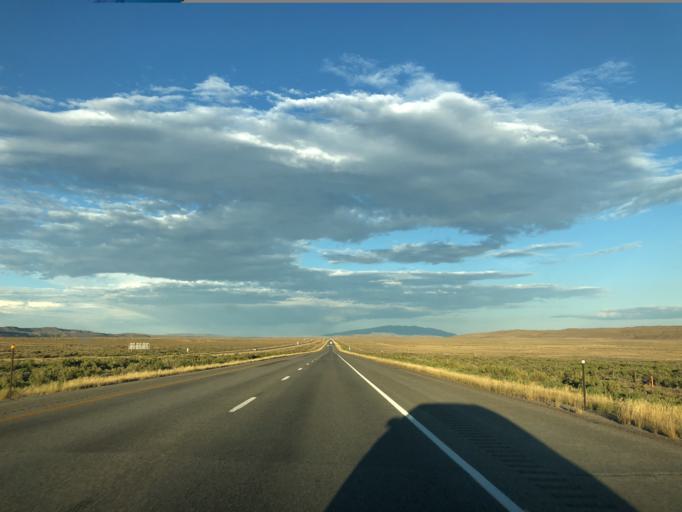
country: US
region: Wyoming
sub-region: Carbon County
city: Rawlins
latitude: 41.7689
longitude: -107.0463
